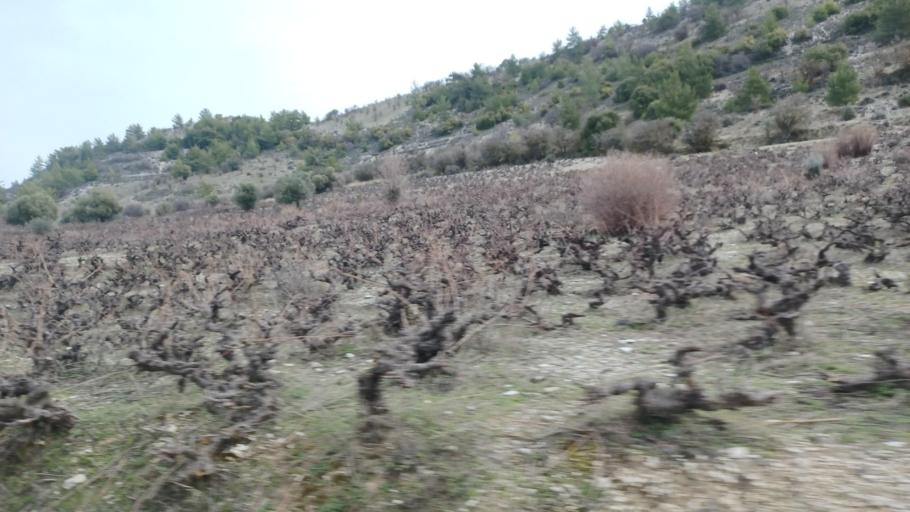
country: CY
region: Limassol
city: Pachna
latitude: 34.8491
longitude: 32.6797
